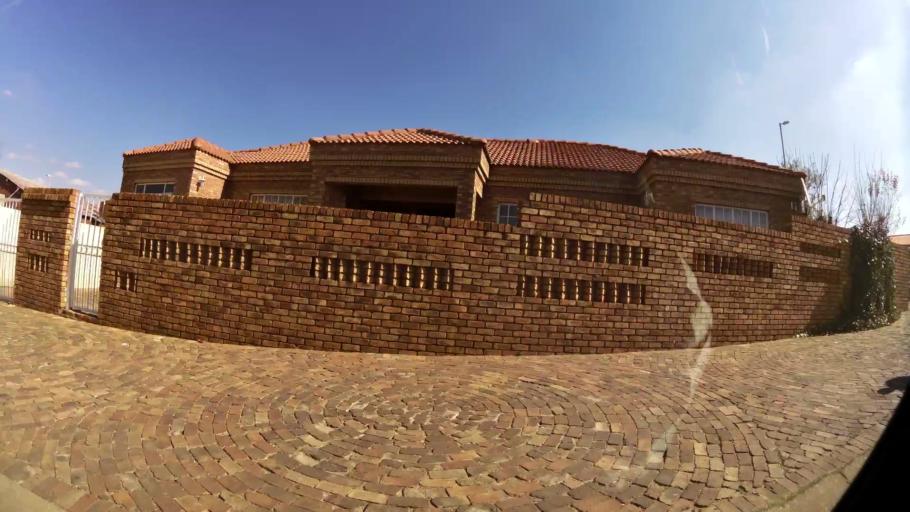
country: ZA
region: Gauteng
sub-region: City of Johannesburg Metropolitan Municipality
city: Soweto
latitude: -26.2416
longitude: 27.9060
